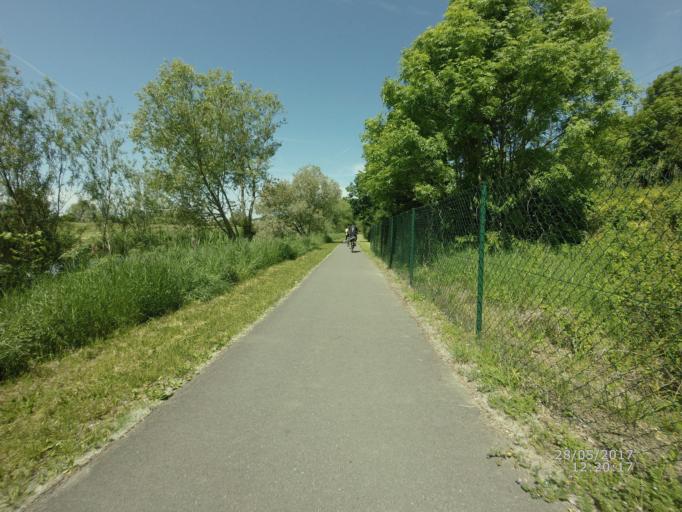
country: DE
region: Thuringia
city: Etzleben
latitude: 51.2861
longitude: 11.1716
